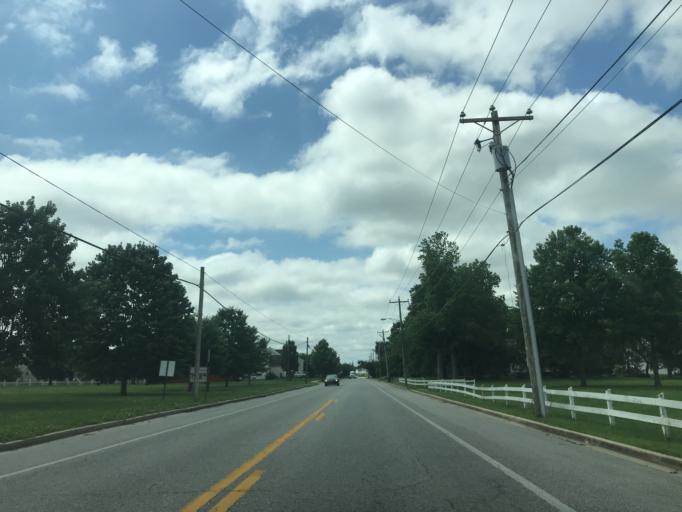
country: US
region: Maryland
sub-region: Caroline County
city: Ridgely
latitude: 38.9527
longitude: -75.8861
